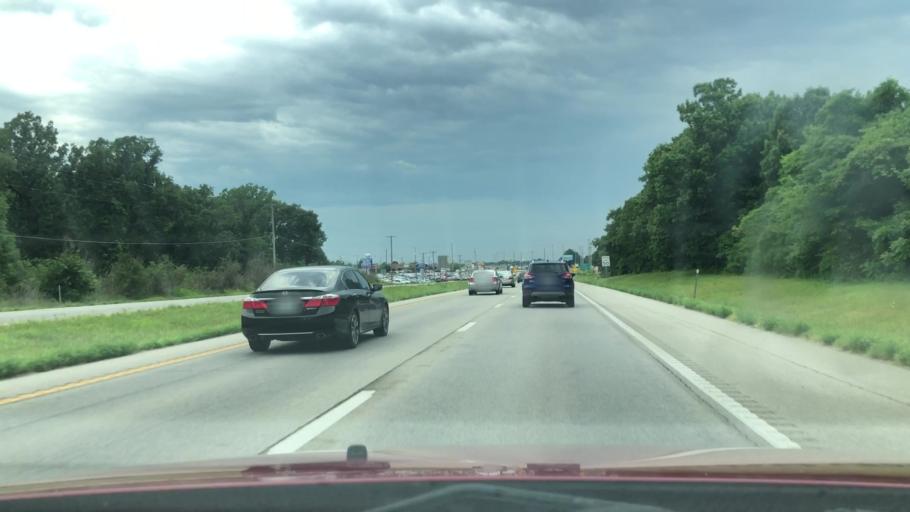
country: US
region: Missouri
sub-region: Greene County
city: Republic
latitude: 37.1378
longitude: -93.4478
